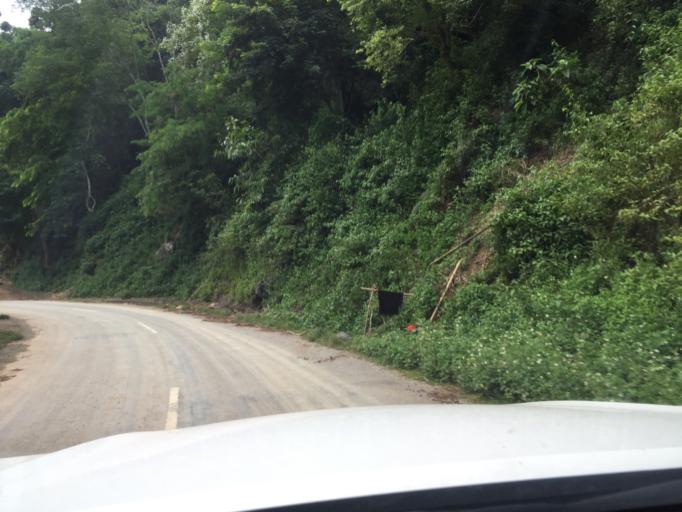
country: LA
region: Oudomxai
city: Muang La
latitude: 21.1106
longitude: 102.2088
